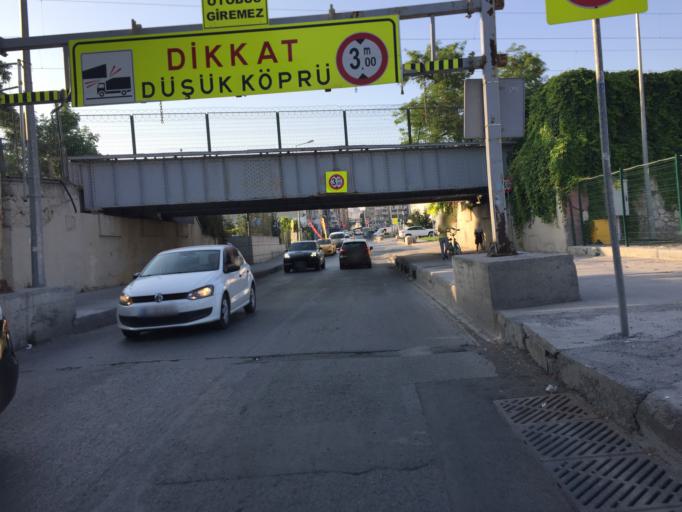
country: TR
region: Istanbul
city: Istanbul
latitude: 41.0042
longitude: 28.9502
